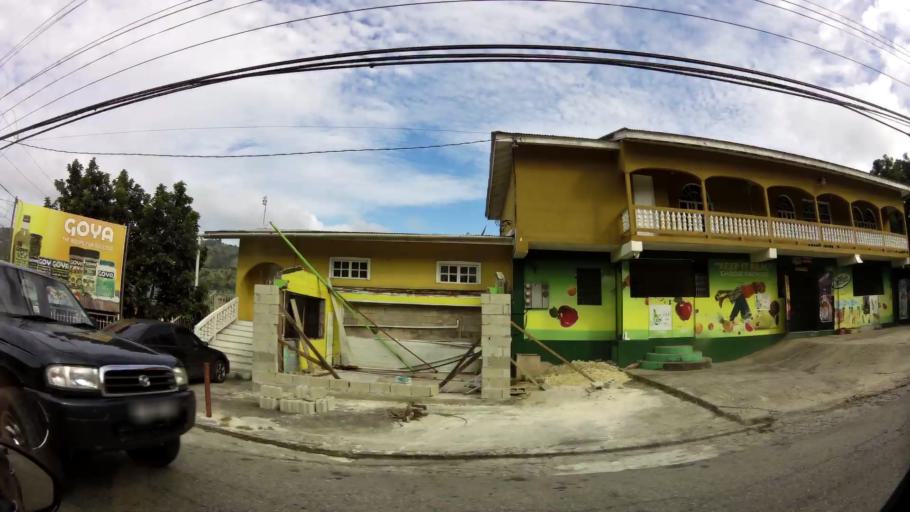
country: TT
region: Diego Martin
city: Petit Valley
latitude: 10.7133
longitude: -61.5016
